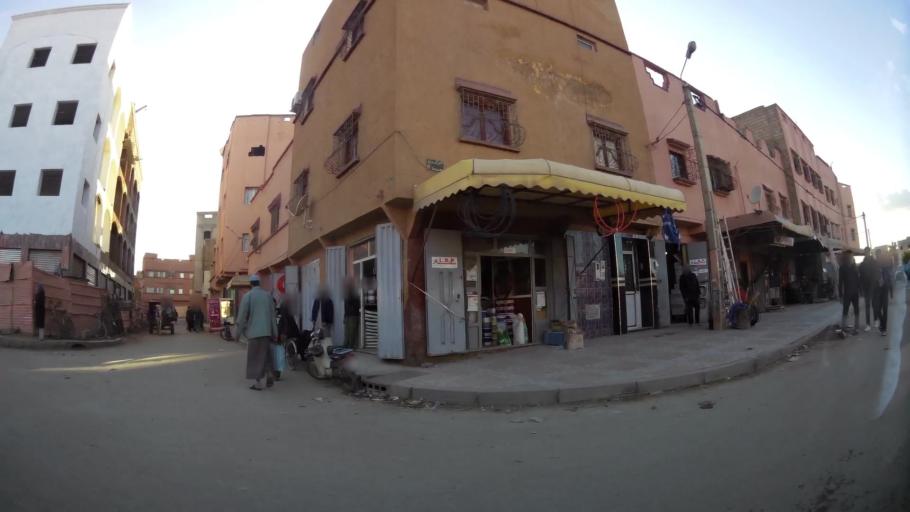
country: MA
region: Marrakech-Tensift-Al Haouz
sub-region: Kelaa-Des-Sraghna
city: Sidi Abdallah
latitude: 32.2447
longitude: -7.9483
